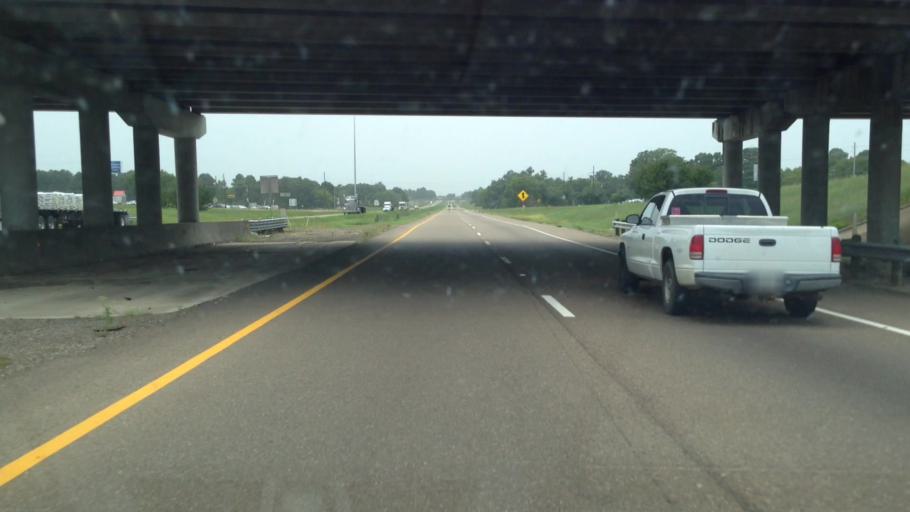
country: US
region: Texas
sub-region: Bowie County
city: New Boston
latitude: 33.4745
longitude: -94.4097
